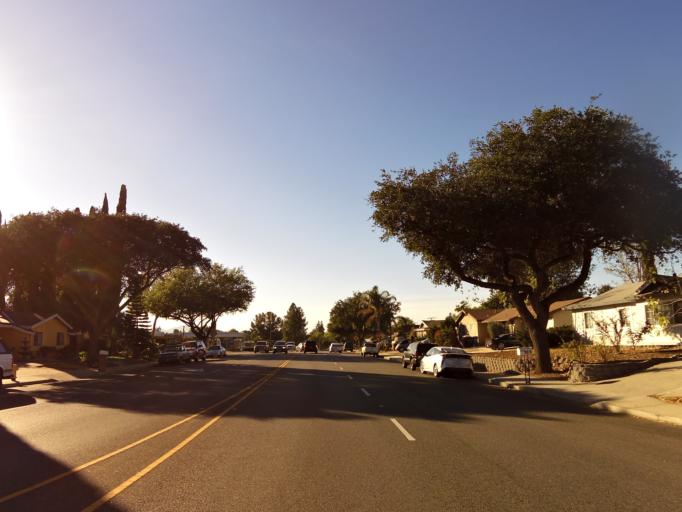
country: US
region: California
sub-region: Ventura County
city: Thousand Oaks
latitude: 34.2154
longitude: -118.8585
